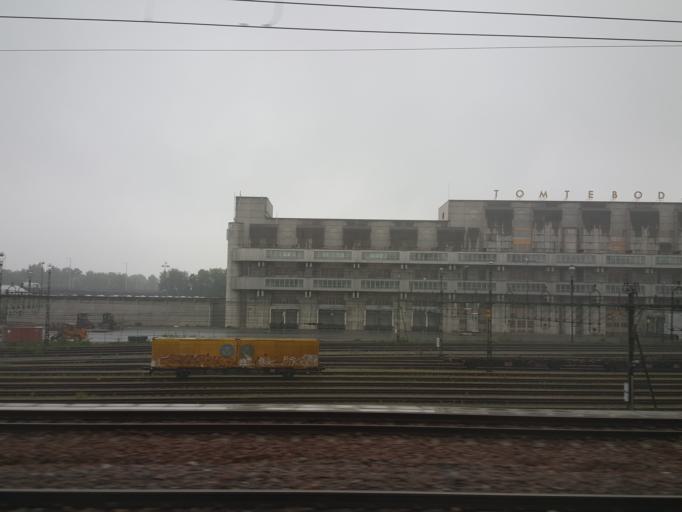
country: SE
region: Stockholm
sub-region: Solna Kommun
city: Solna
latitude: 59.3475
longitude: 18.0188
